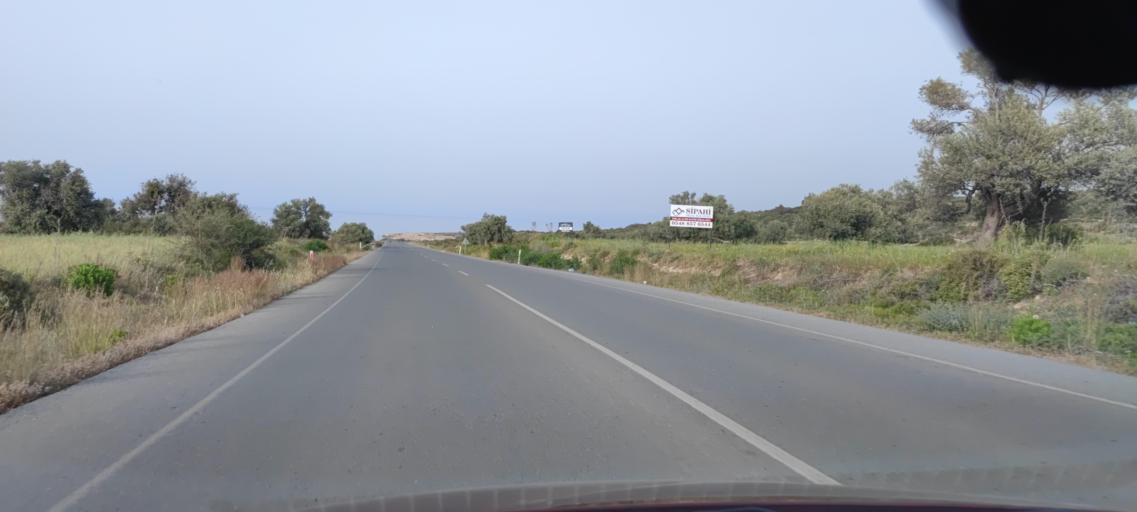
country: CY
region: Ammochostos
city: Leonarisso
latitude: 35.5498
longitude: 34.2076
